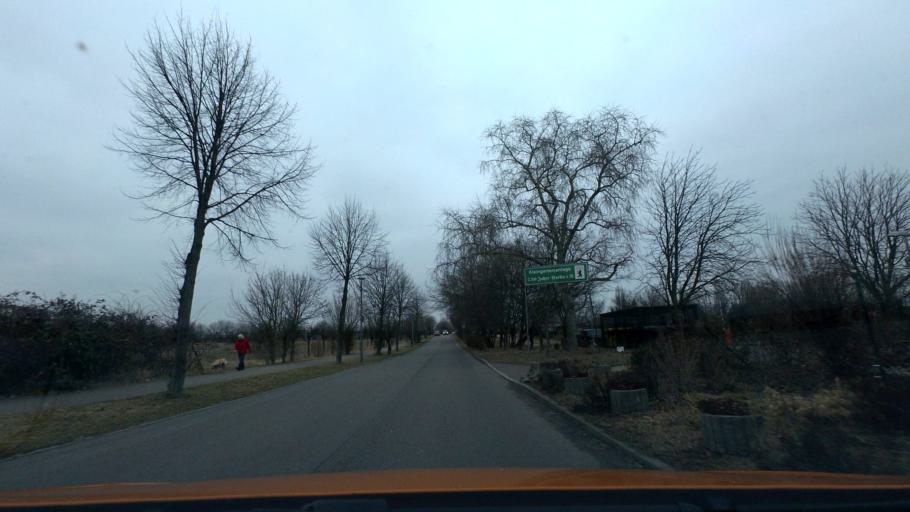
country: DE
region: Berlin
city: Falkenberg
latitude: 52.5716
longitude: 13.5458
